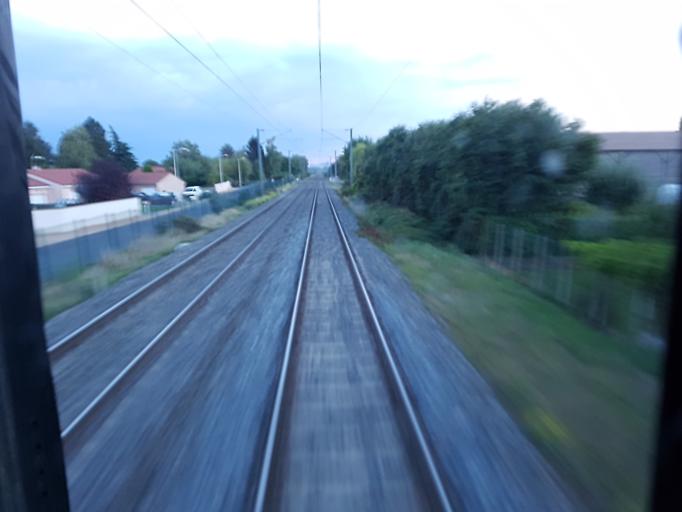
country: FR
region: Auvergne
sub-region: Departement du Puy-de-Dome
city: Menetrol
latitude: 45.8727
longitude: 3.1273
